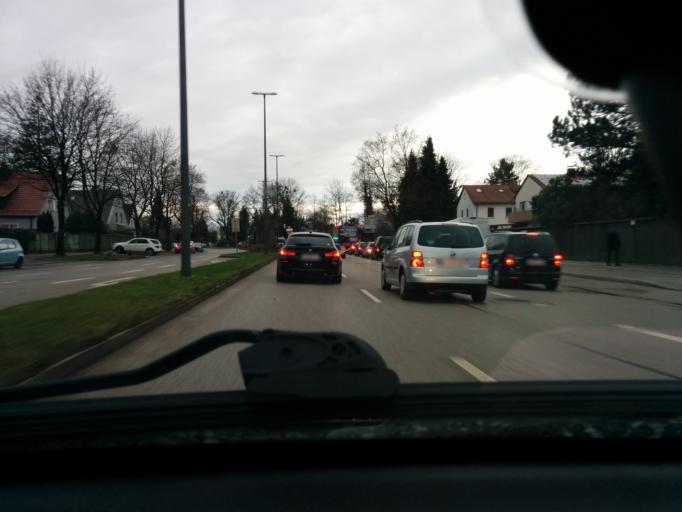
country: DE
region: Bavaria
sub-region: Upper Bavaria
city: Karlsfeld
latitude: 48.1796
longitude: 11.4893
